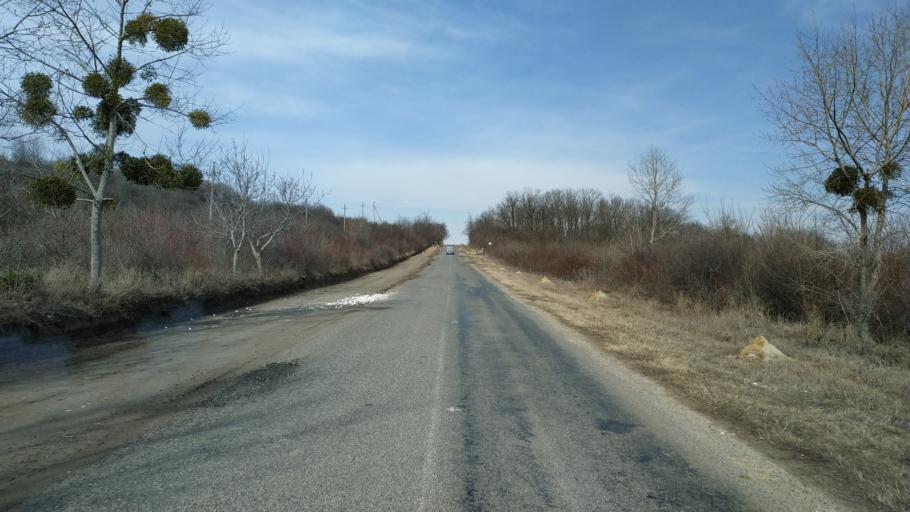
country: MD
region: Nisporeni
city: Nisporeni
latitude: 47.1889
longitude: 28.0698
